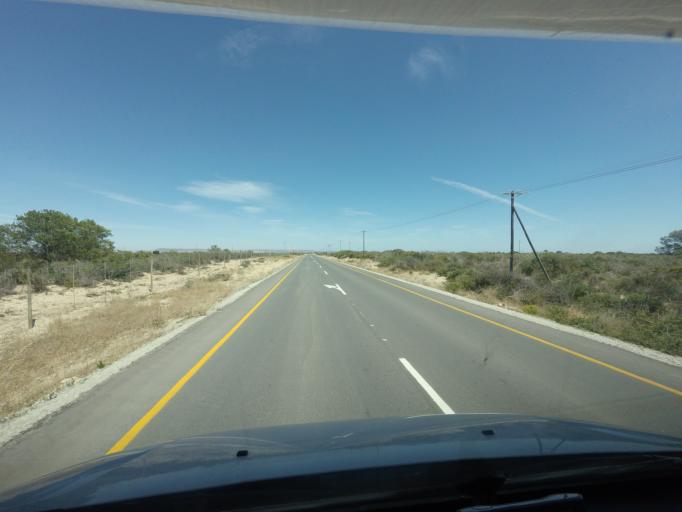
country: ZA
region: Western Cape
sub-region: West Coast District Municipality
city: Vredenburg
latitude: -32.7940
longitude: 18.2370
